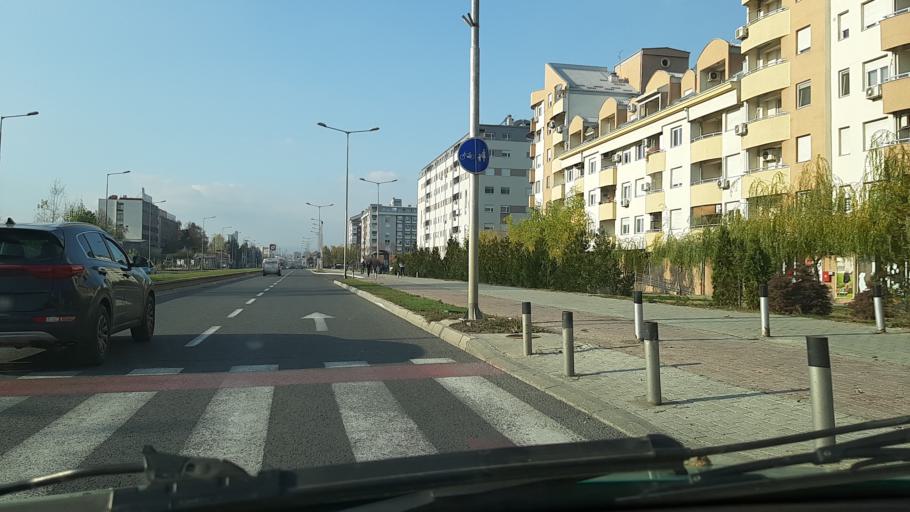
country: MK
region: Kisela Voda
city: Usje
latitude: 41.9802
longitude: 21.4583
